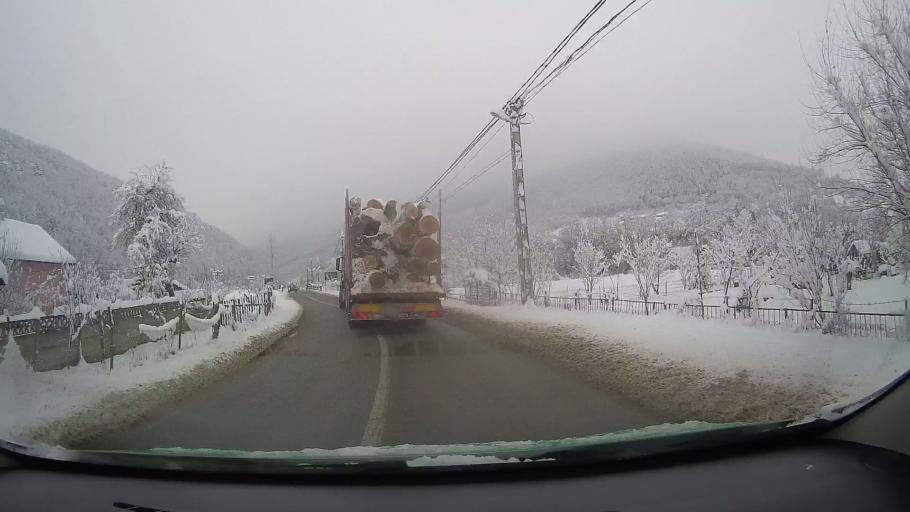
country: RO
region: Sibiu
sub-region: Comuna Orlat
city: Orlat
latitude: 45.7657
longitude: 23.9400
